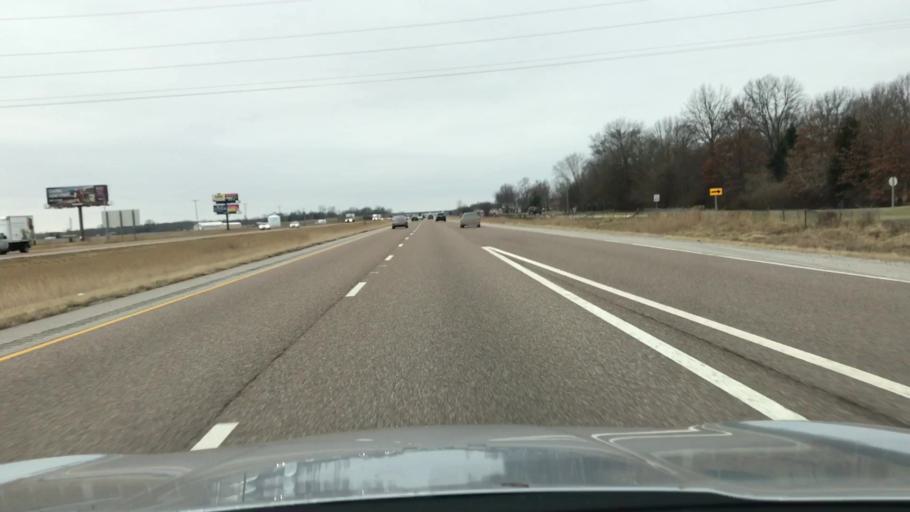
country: US
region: Illinois
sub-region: Macoupin County
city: Staunton
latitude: 38.9650
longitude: -89.7572
